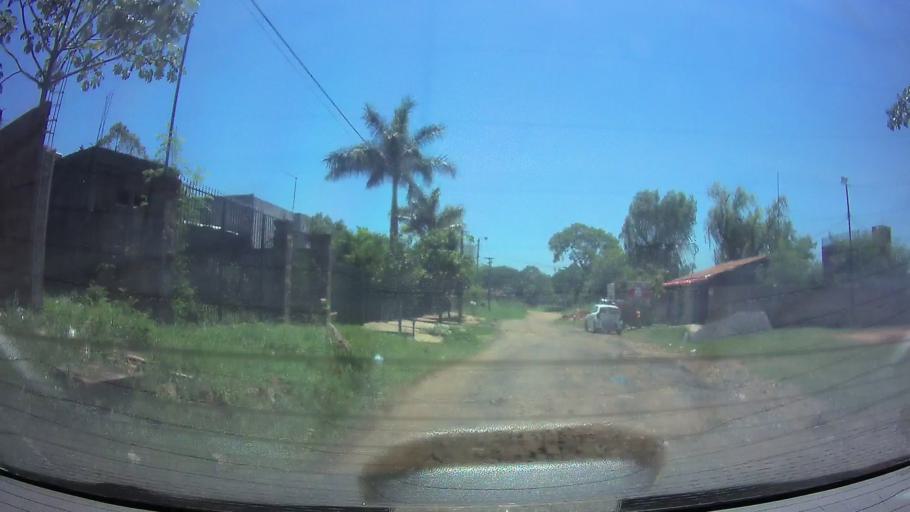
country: PY
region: Central
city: San Lorenzo
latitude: -25.3466
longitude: -57.4904
